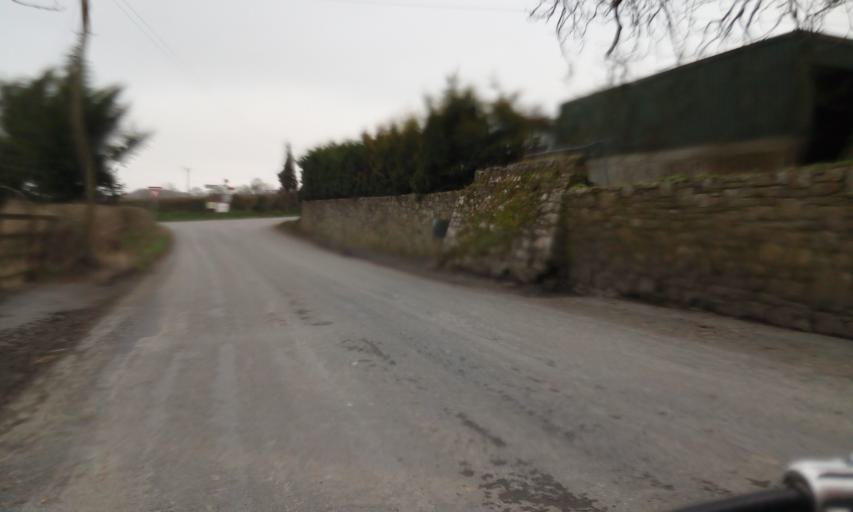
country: IE
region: Leinster
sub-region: Kilkenny
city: Kilkenny
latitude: 52.6598
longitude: -7.1456
